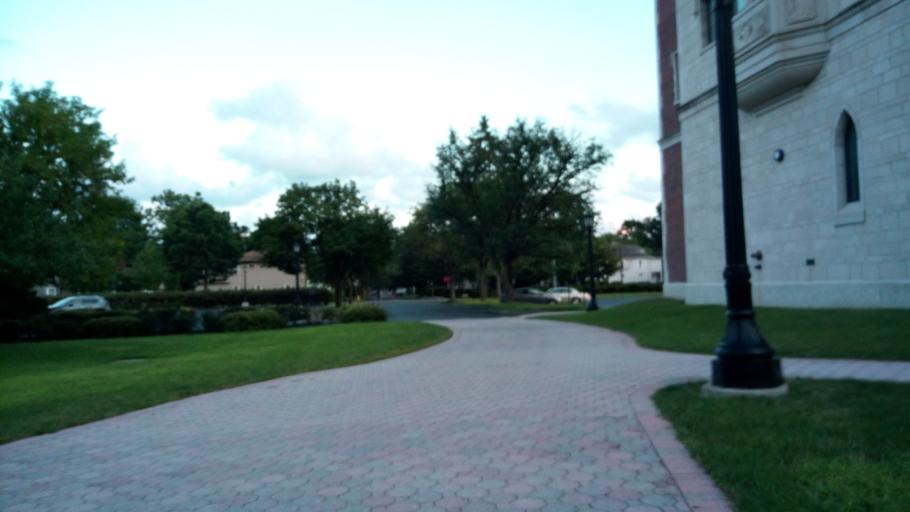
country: US
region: New York
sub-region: Chemung County
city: Elmira
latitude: 42.0955
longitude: -76.8155
